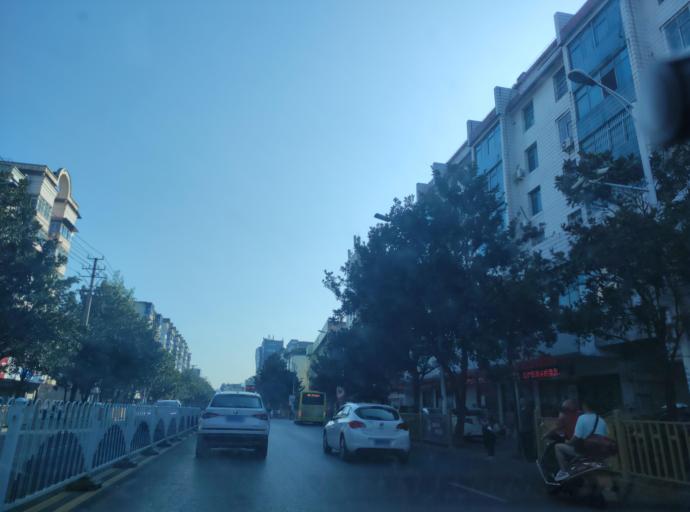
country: CN
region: Jiangxi Sheng
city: Pingxiang
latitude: 27.6309
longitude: 113.8522
